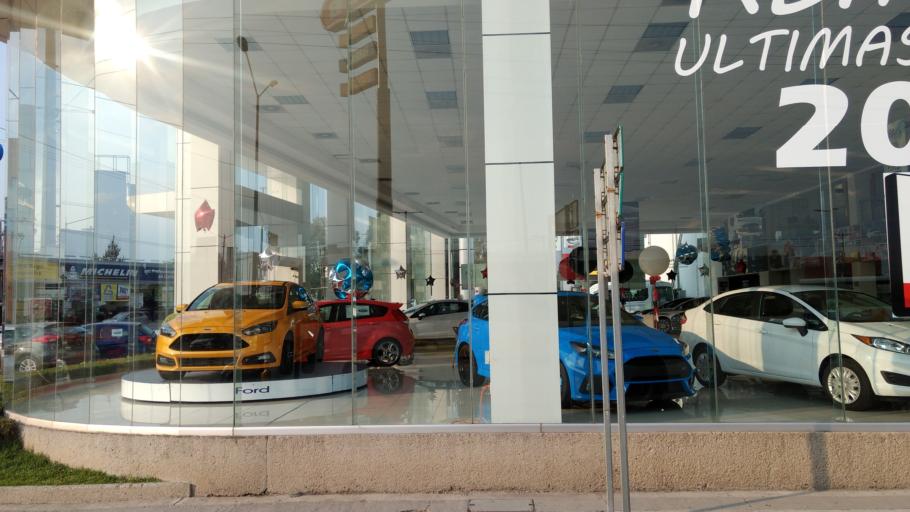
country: MX
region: Guanajuato
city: Leon
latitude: 21.1473
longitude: -101.6848
